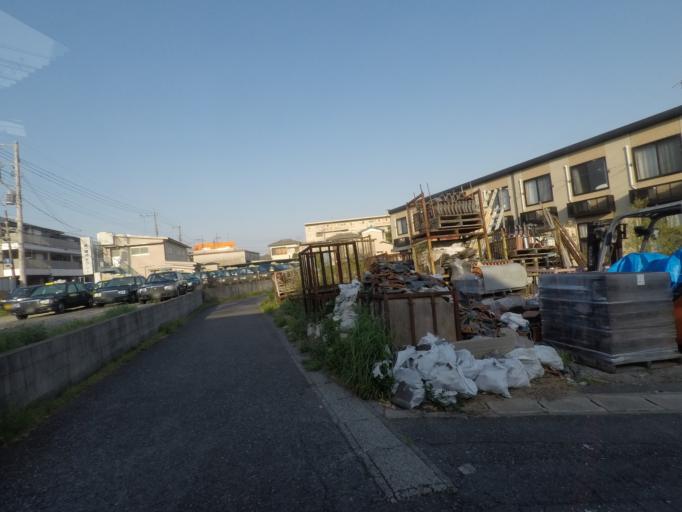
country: JP
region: Chiba
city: Chiba
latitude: 35.6173
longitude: 140.1415
